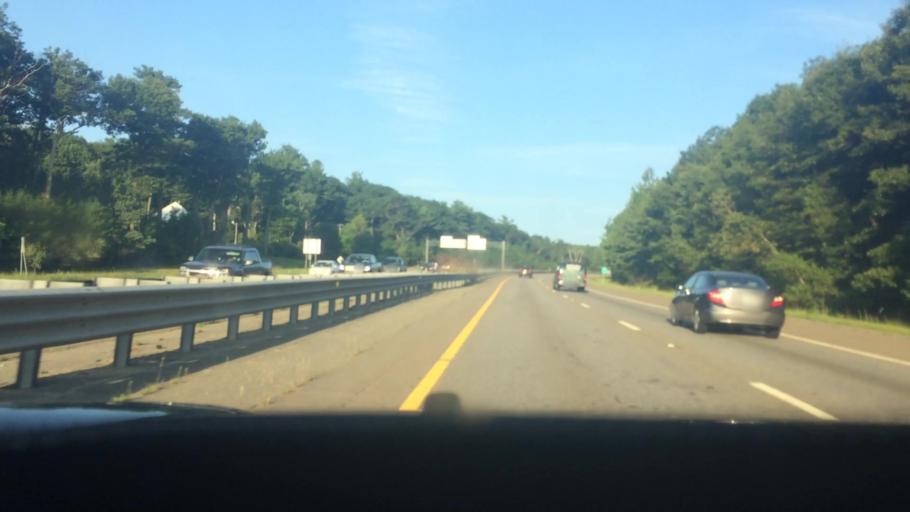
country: US
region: Massachusetts
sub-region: Worcester County
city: Westminster
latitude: 42.5421
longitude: -71.8849
